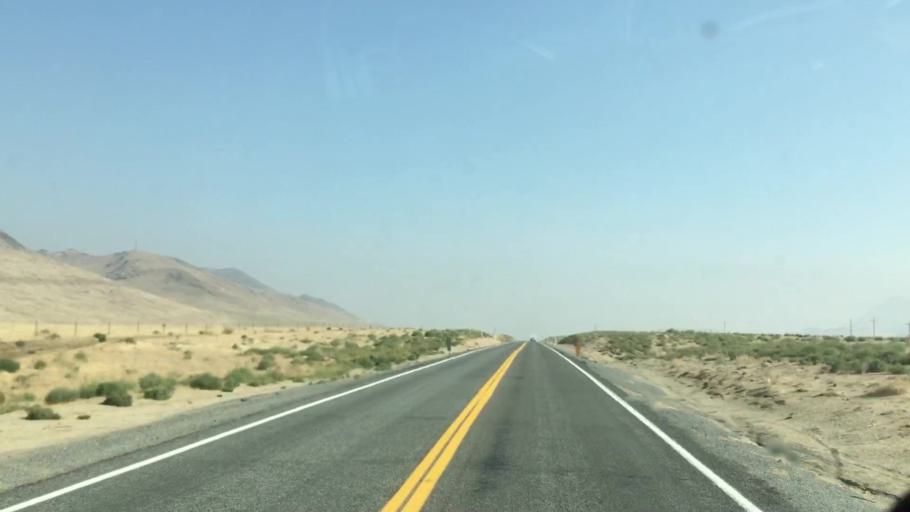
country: US
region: Nevada
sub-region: Lyon County
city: Fernley
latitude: 40.3858
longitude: -119.3335
